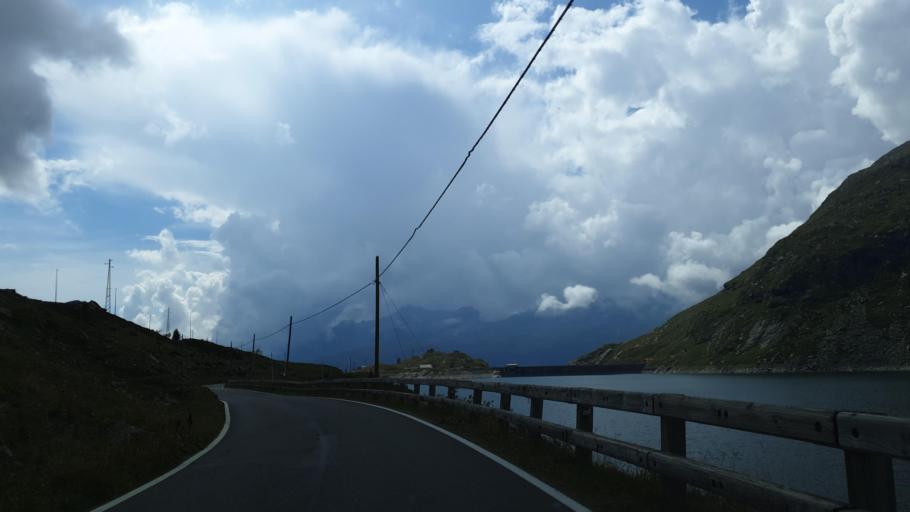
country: IT
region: Lombardy
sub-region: Provincia di Sondrio
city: Campodolcino
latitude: 46.4804
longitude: 9.3542
